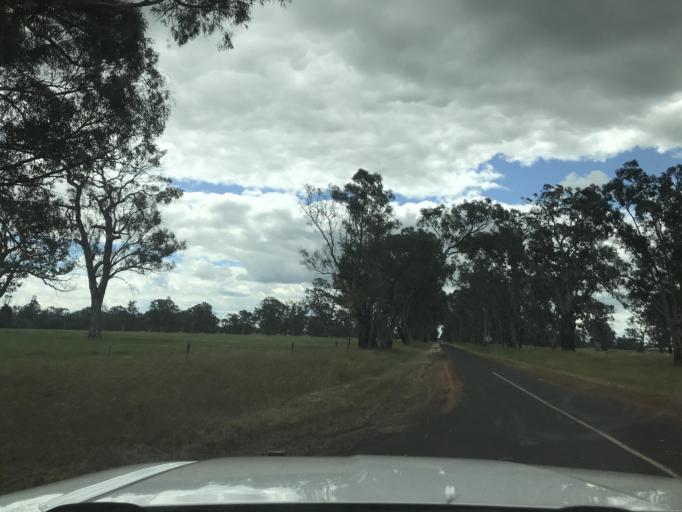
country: AU
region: South Australia
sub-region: Wattle Range
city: Penola
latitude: -37.0783
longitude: 141.1825
